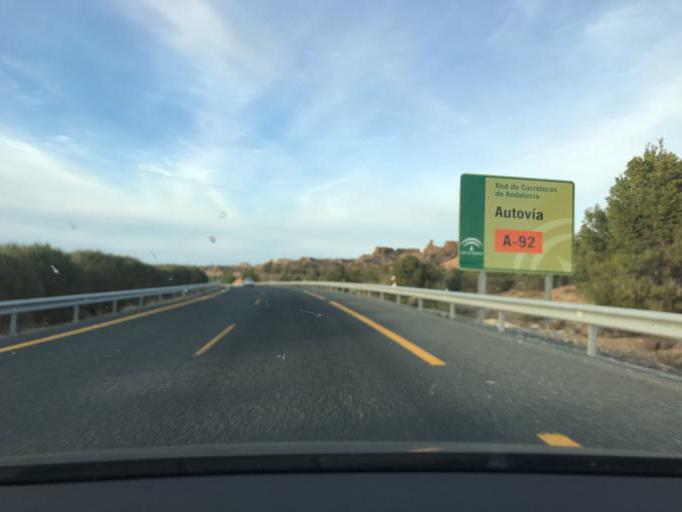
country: ES
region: Andalusia
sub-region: Provincia de Granada
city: Guadix
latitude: 37.2995
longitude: -3.1096
